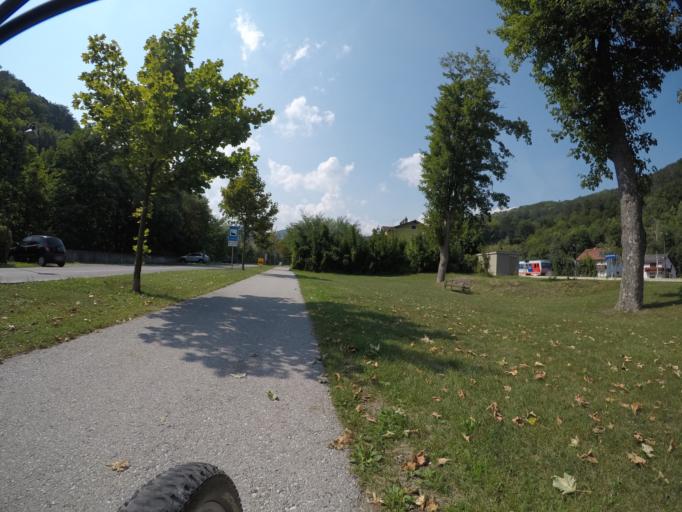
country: AT
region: Lower Austria
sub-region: Politischer Bezirk Baden
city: Weissenbach an der Triesting
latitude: 47.9839
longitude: 16.0467
